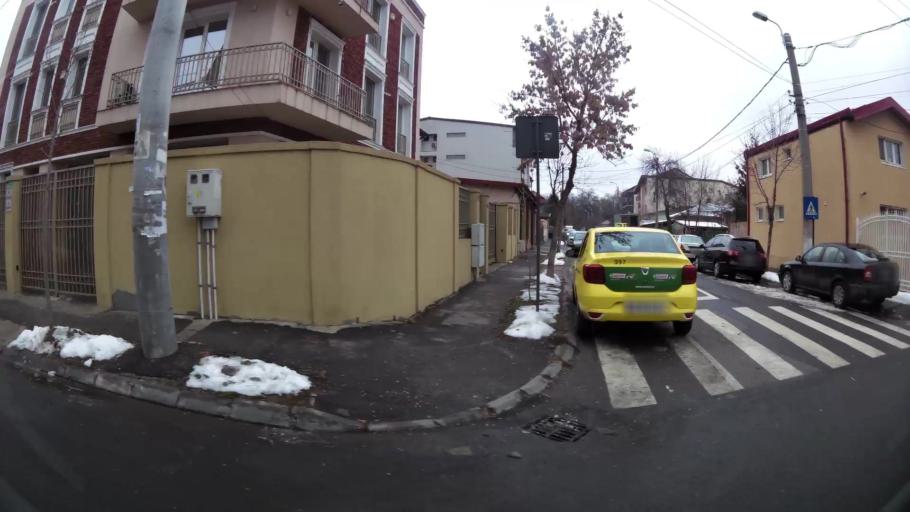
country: RO
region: Ilfov
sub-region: Comuna Chiajna
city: Rosu
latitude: 44.4877
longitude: 26.0300
